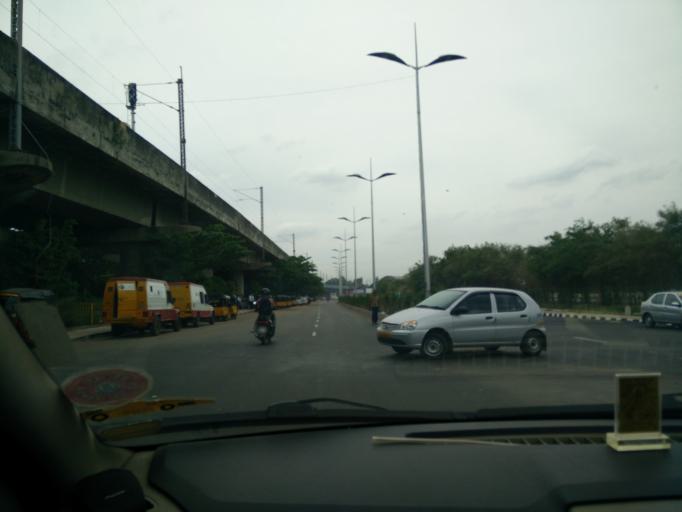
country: IN
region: Tamil Nadu
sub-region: Chennai
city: Chennai
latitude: 13.0698
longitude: 80.2775
